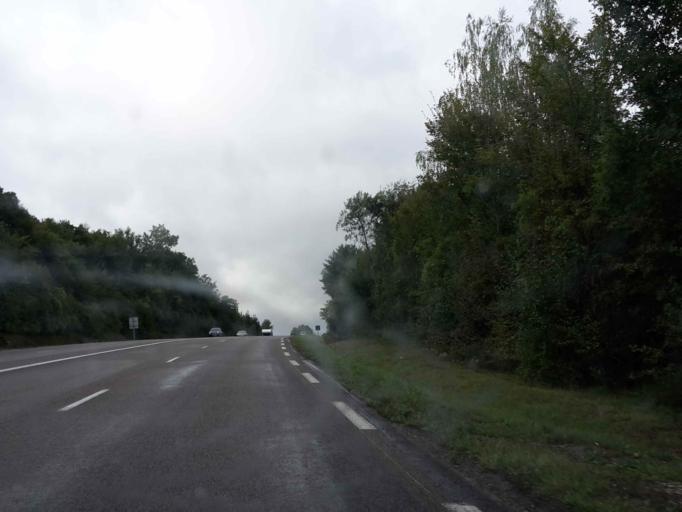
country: FR
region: Franche-Comte
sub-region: Departement du Doubs
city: Roulans
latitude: 47.3267
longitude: 6.2621
